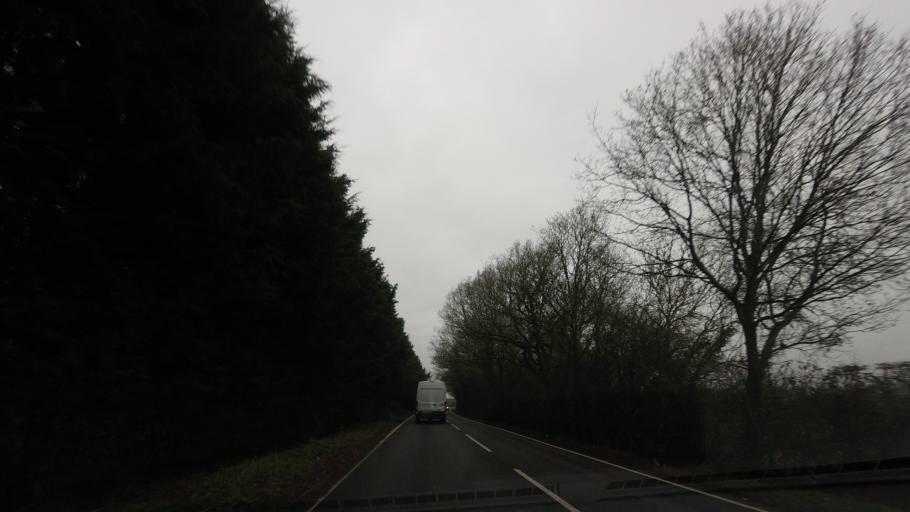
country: GB
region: England
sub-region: Kent
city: Staplehurst
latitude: 51.1439
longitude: 0.5516
